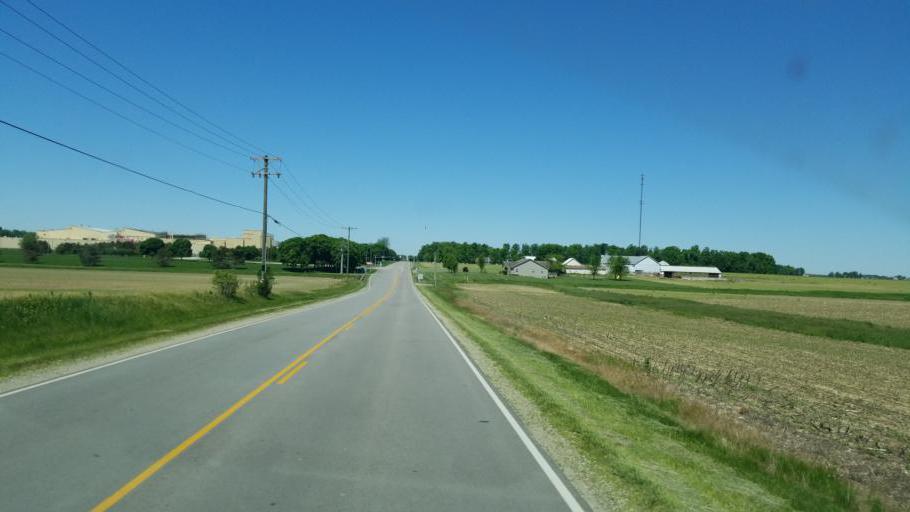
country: US
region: Ohio
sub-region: Shelby County
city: Anna
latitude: 40.3806
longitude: -84.1826
